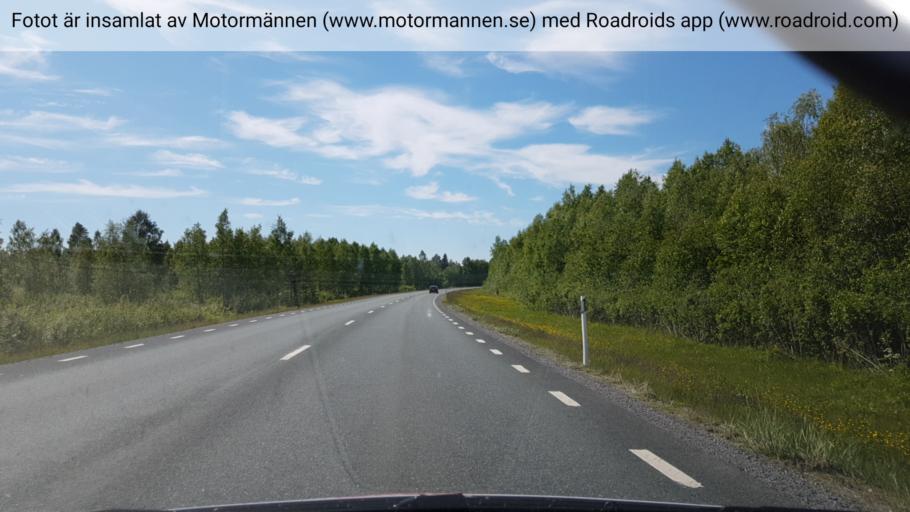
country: SE
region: Norrbotten
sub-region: Haparanda Kommun
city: Haparanda
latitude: 65.8242
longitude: 24.0656
